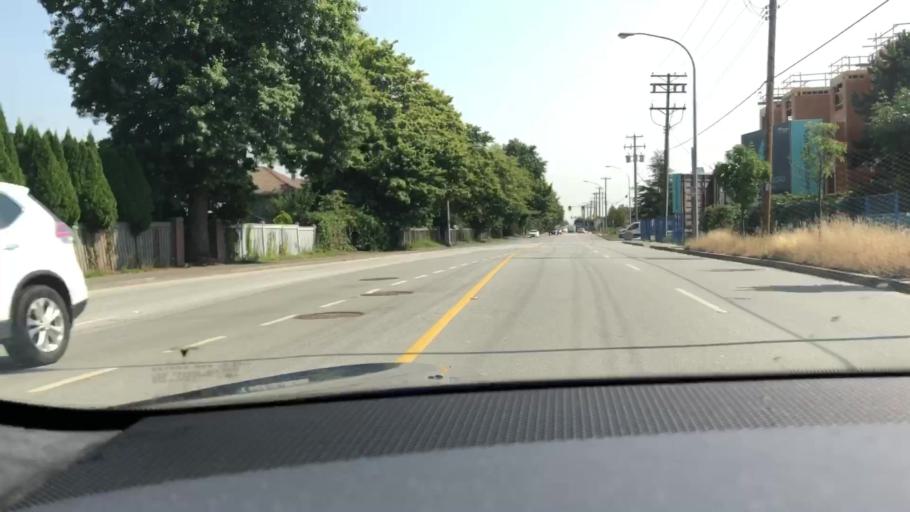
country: CA
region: British Columbia
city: Richmond
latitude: 49.1847
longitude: -123.1190
